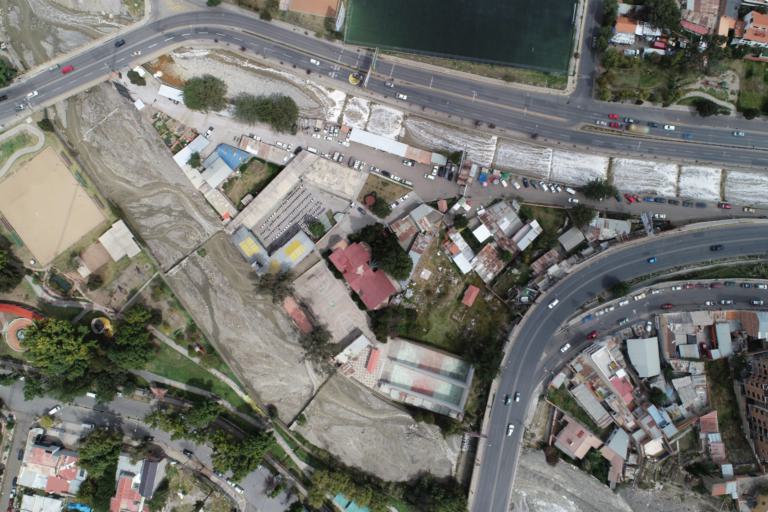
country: BO
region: La Paz
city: La Paz
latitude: -16.5423
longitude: -68.0932
